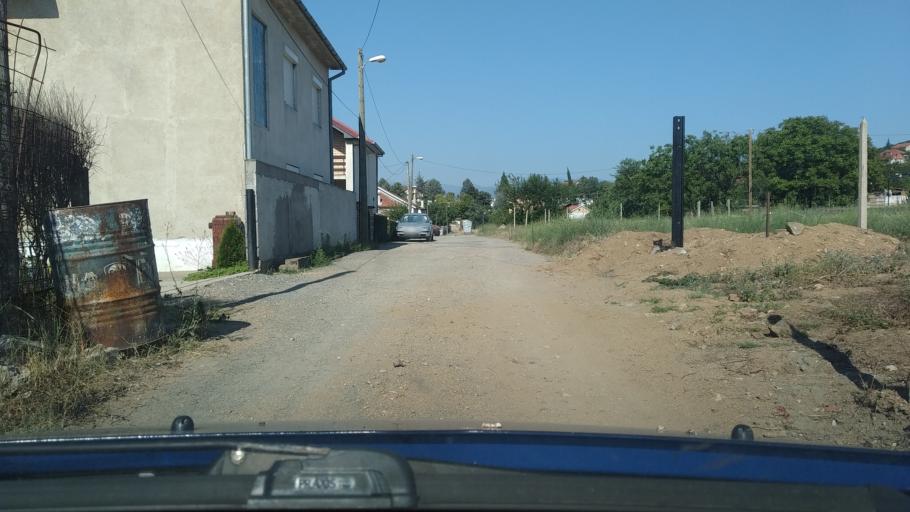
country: MK
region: Bogdanci
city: Bogdanci
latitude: 41.2052
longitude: 22.5849
